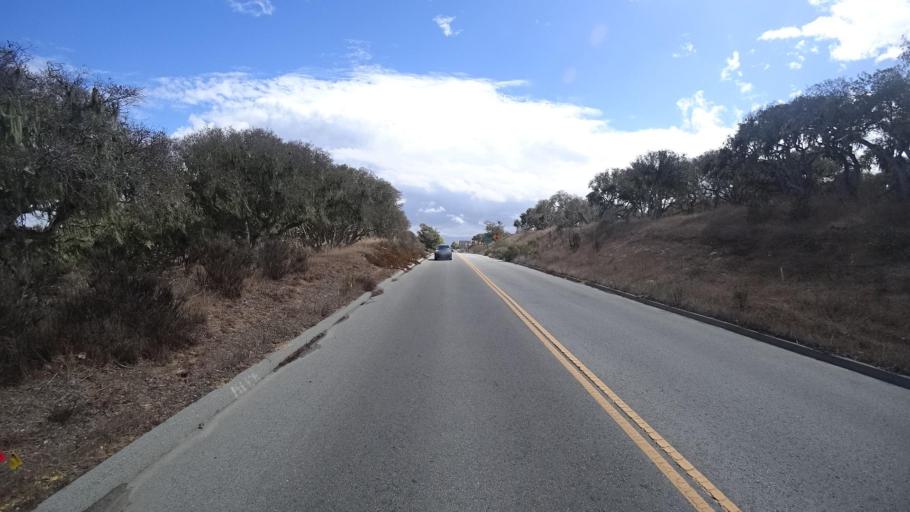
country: US
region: California
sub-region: Monterey County
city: Marina
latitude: 36.6551
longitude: -121.7454
